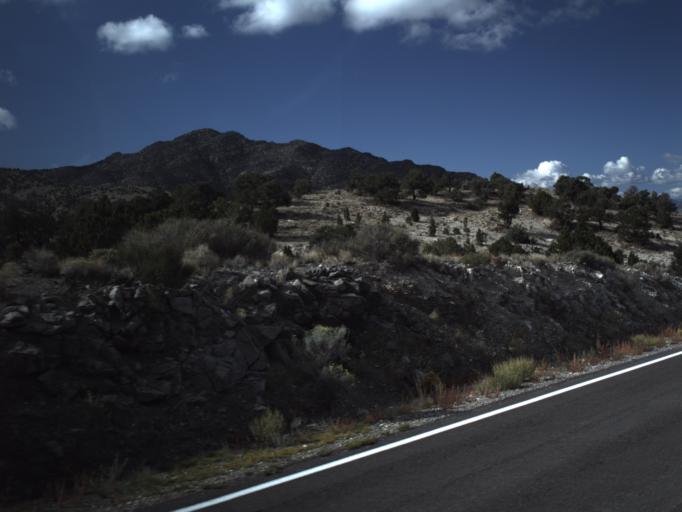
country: US
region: Utah
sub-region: Beaver County
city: Milford
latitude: 38.5163
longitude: -113.5557
